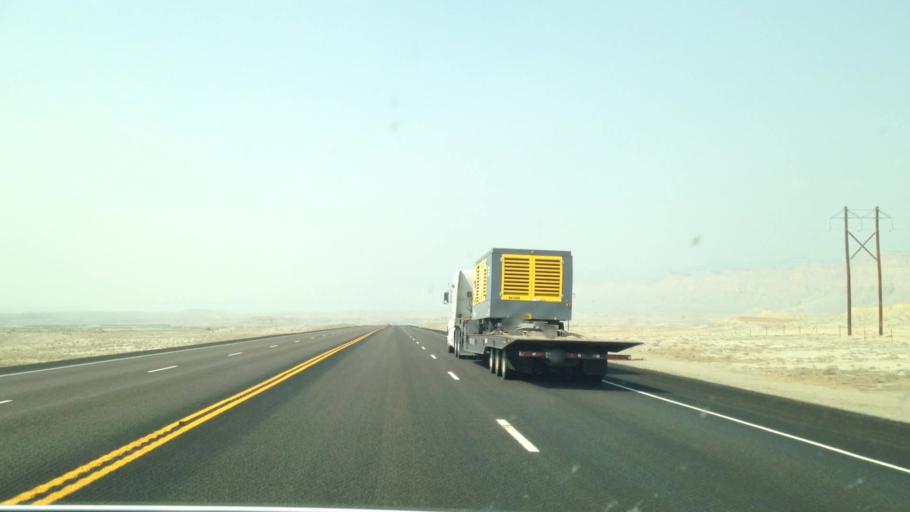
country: US
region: Utah
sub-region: Carbon County
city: East Carbon City
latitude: 39.2141
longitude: -110.3383
